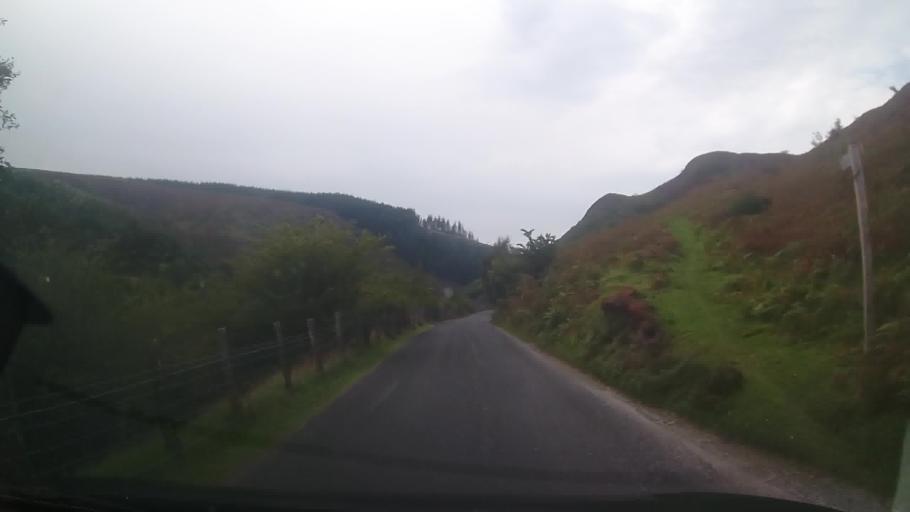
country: GB
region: Wales
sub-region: Sir Powys
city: Rhayader
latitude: 52.2790
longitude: -3.5935
